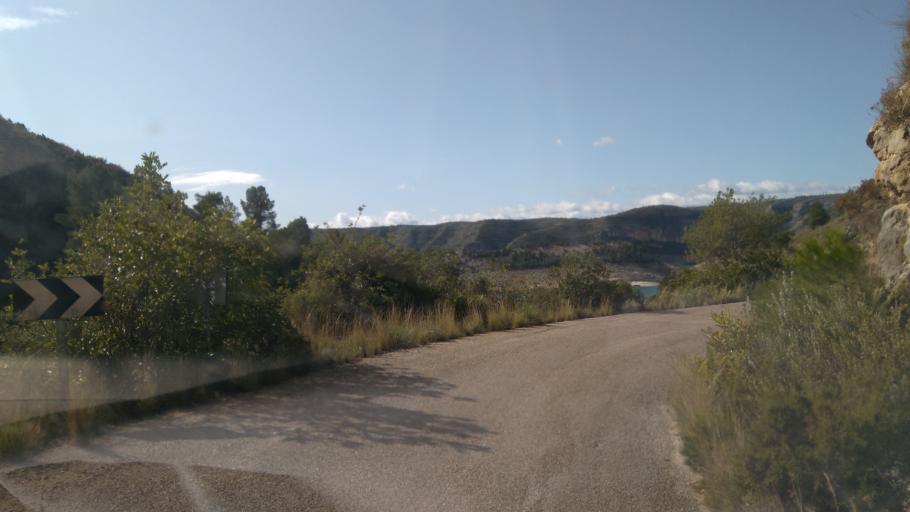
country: ES
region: Valencia
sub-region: Provincia de Valencia
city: Sumacarcer
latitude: 39.1529
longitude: -0.6518
